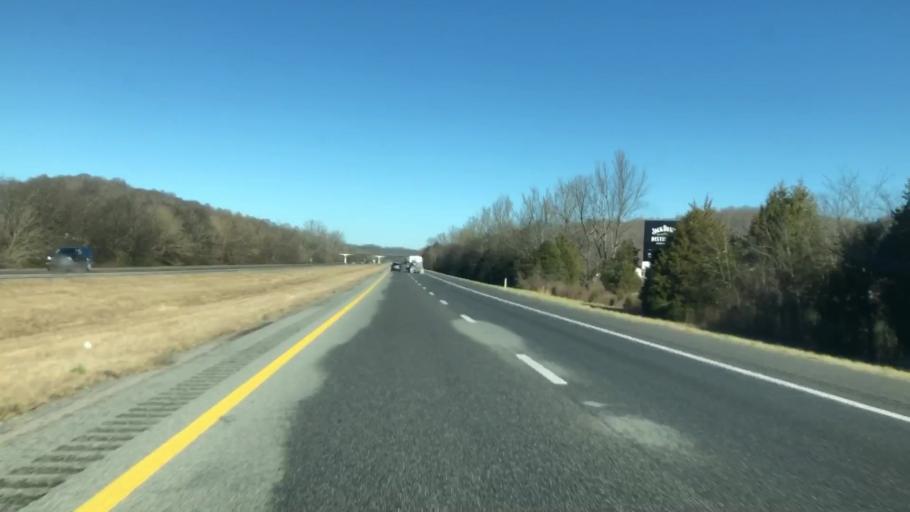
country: US
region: Alabama
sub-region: Limestone County
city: Ardmore
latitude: 35.1314
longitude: -86.8799
